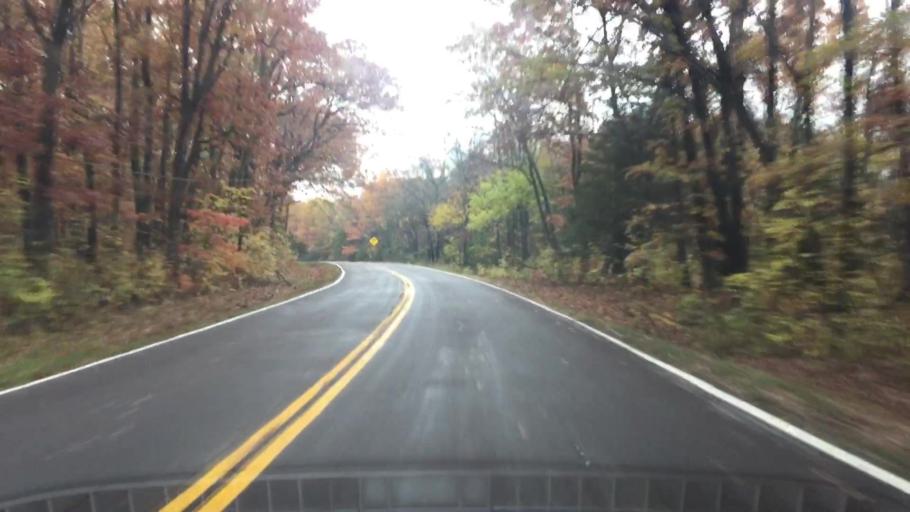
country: US
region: Missouri
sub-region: Boone County
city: Columbia
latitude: 38.8694
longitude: -92.3190
